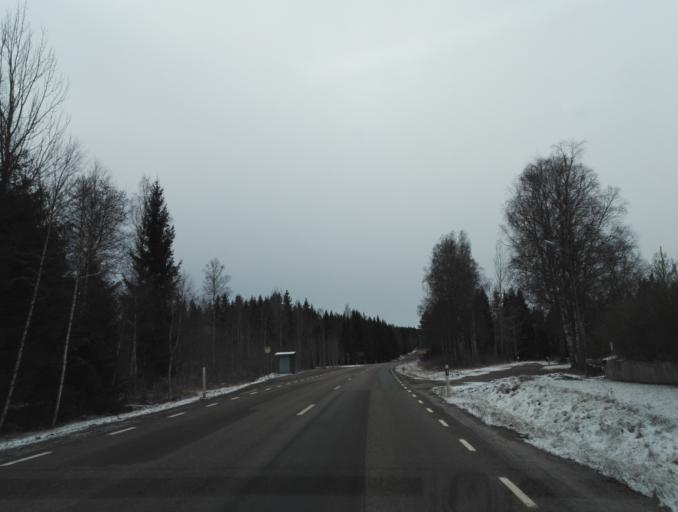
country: SE
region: Kalmar
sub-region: Hultsfreds Kommun
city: Virserum
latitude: 57.2364
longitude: 15.5407
